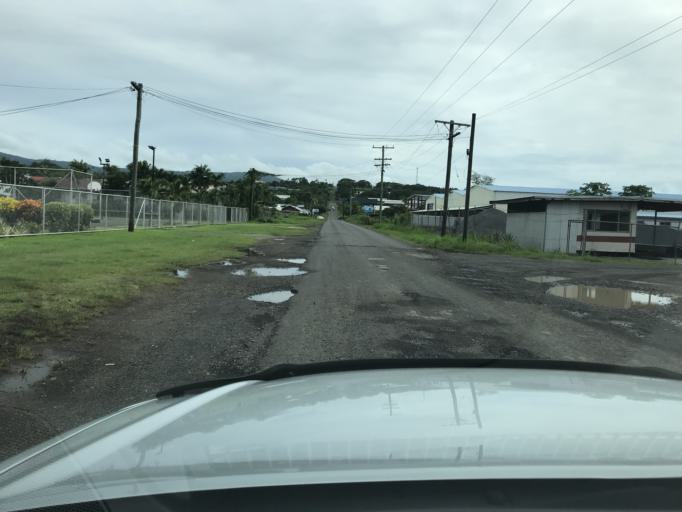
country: WS
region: Tuamasaga
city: Vaiusu
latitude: -13.8242
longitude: -171.8075
